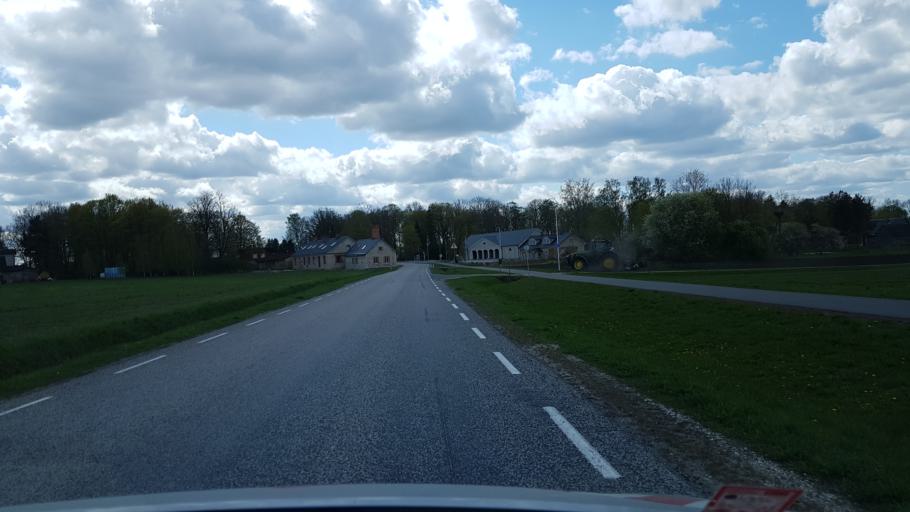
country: EE
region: Jogevamaa
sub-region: Poltsamaa linn
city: Poltsamaa
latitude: 58.7089
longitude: 25.9404
